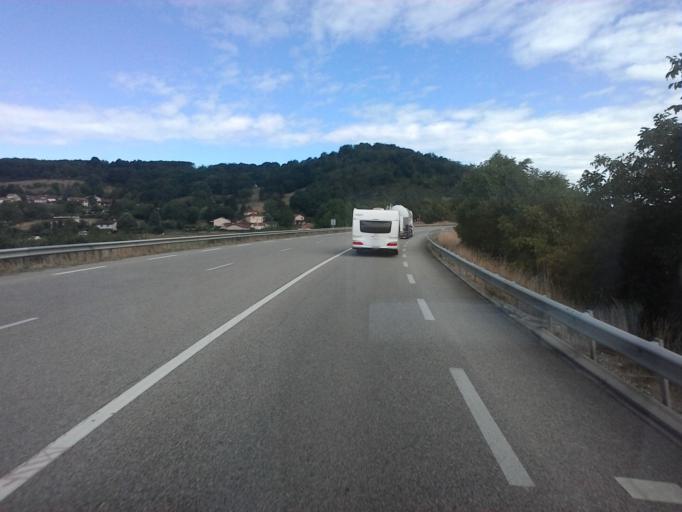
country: FR
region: Rhone-Alpes
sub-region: Departement de l'Ain
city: Lagnieu
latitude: 45.8892
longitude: 5.3378
